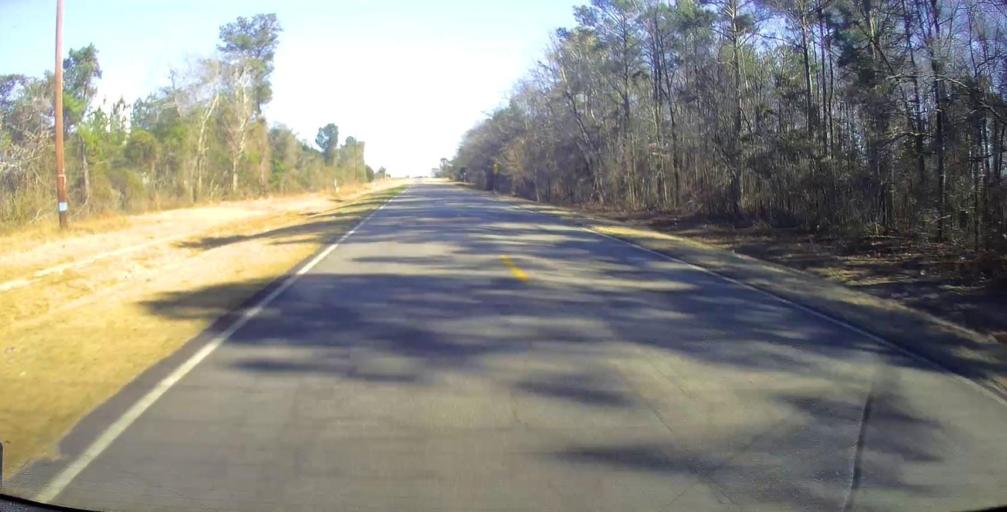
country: US
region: Georgia
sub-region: Taylor County
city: Butler
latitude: 32.5657
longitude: -84.2657
